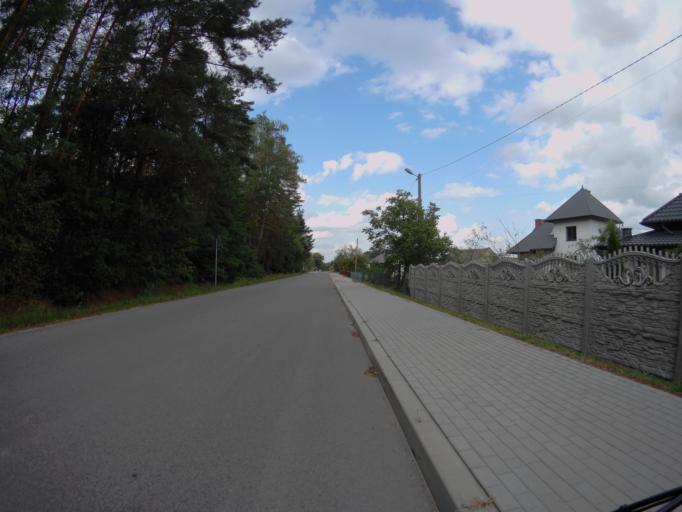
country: PL
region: Subcarpathian Voivodeship
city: Nowa Sarzyna
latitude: 50.2814
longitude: 22.3525
